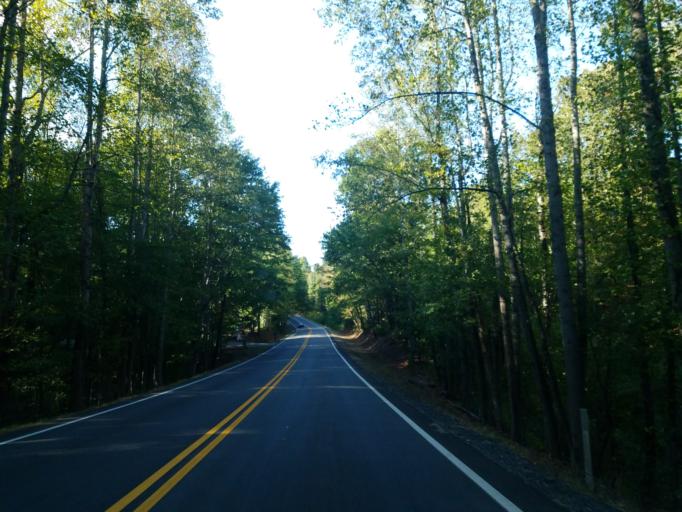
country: US
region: Georgia
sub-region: Bartow County
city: Emerson
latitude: 34.0767
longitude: -84.8311
